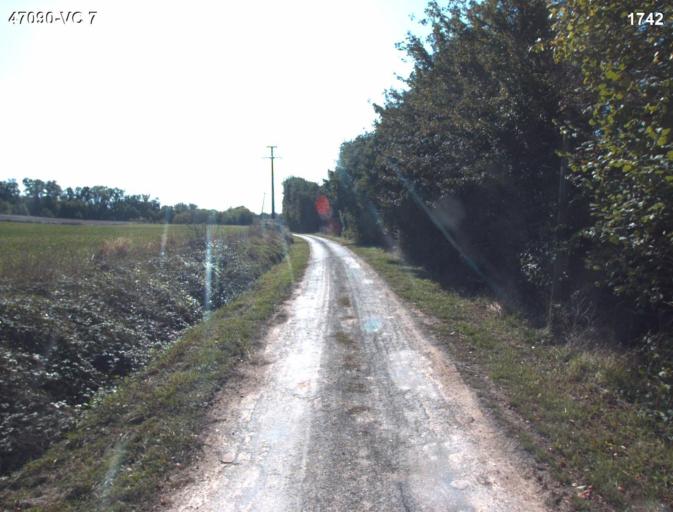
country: FR
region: Aquitaine
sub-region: Departement du Lot-et-Garonne
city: Vianne
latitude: 44.1838
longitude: 0.3580
